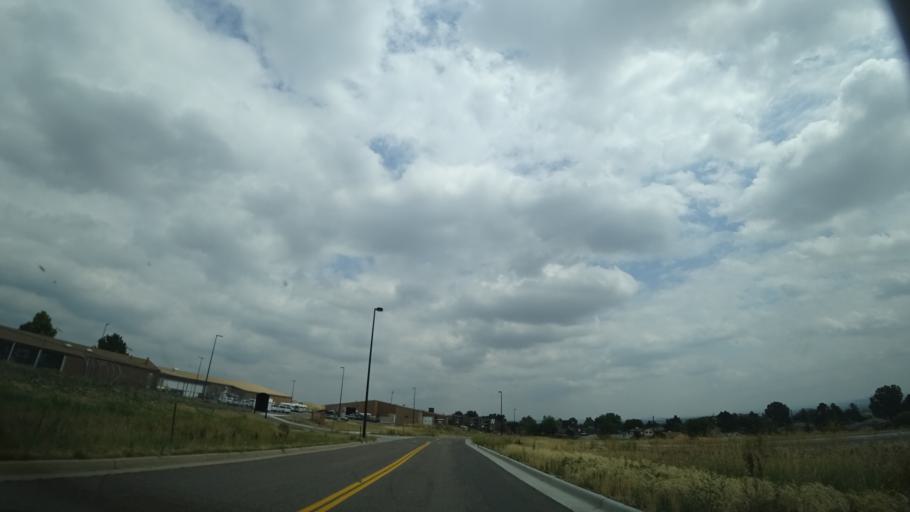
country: US
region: Colorado
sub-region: Jefferson County
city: West Pleasant View
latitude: 39.7144
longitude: -105.1487
